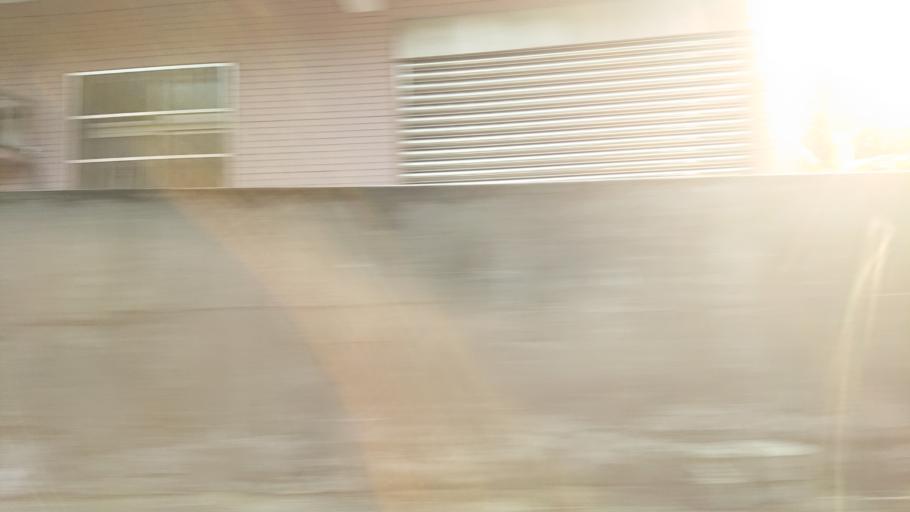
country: TW
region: Taiwan
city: Daxi
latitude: 24.8674
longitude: 121.4150
